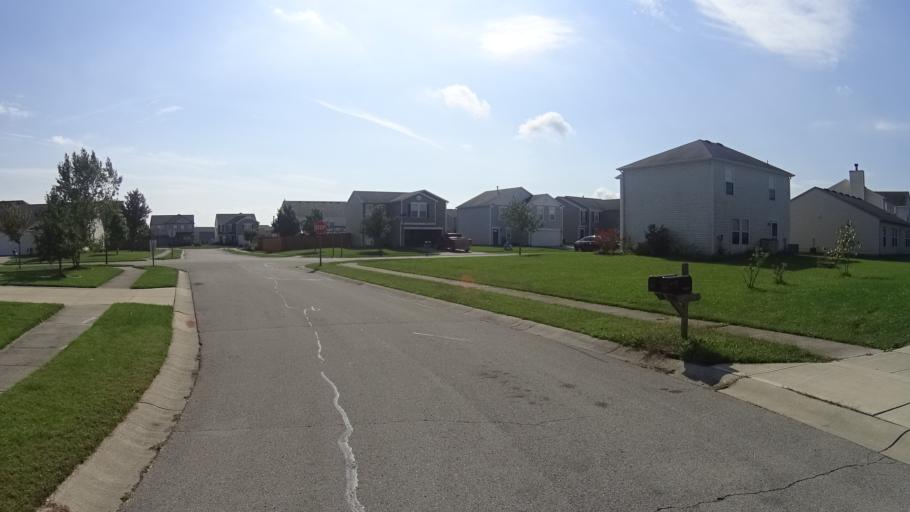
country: US
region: Indiana
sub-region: Hancock County
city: Fortville
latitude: 39.9846
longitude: -85.8569
